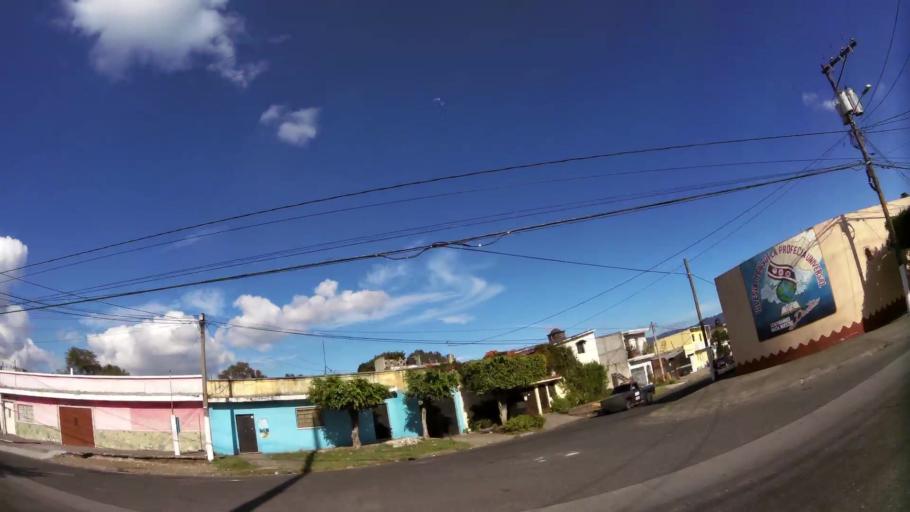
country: GT
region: Guatemala
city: Villa Nueva
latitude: 14.5194
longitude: -90.5739
